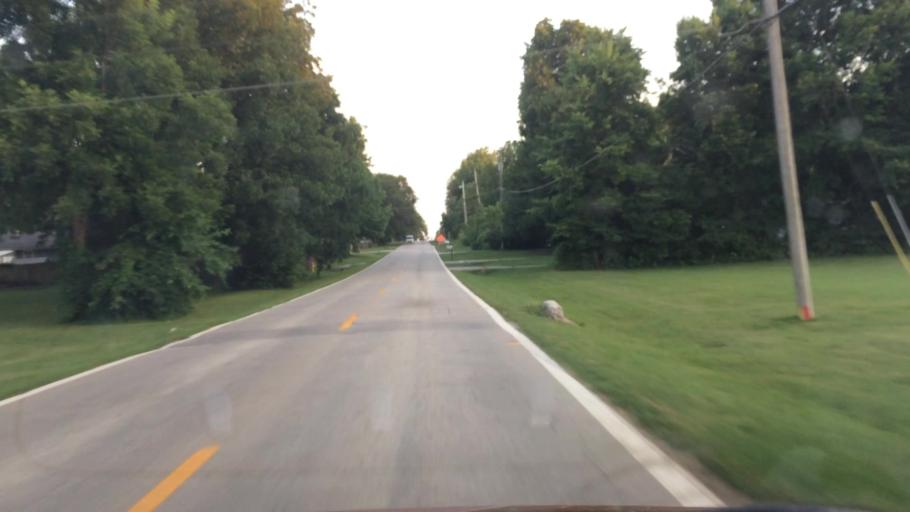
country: US
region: Missouri
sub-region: Greene County
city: Springfield
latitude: 37.2104
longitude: -93.3740
